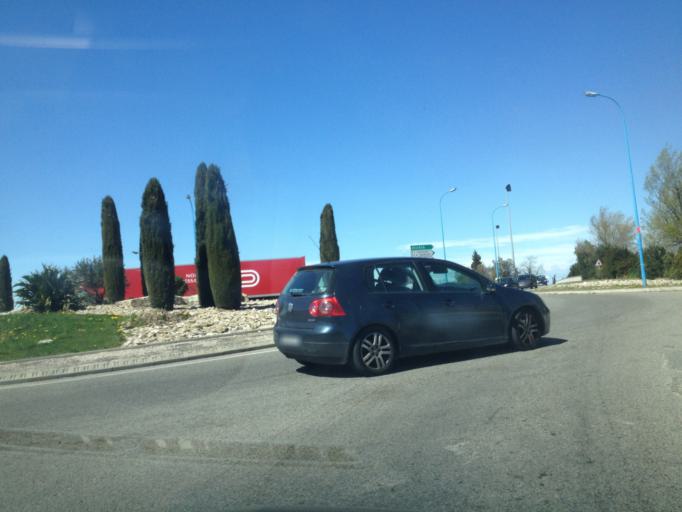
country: FR
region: Provence-Alpes-Cote d'Azur
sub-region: Departement du Vaucluse
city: Le Pontet
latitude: 43.9730
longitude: 4.8671
